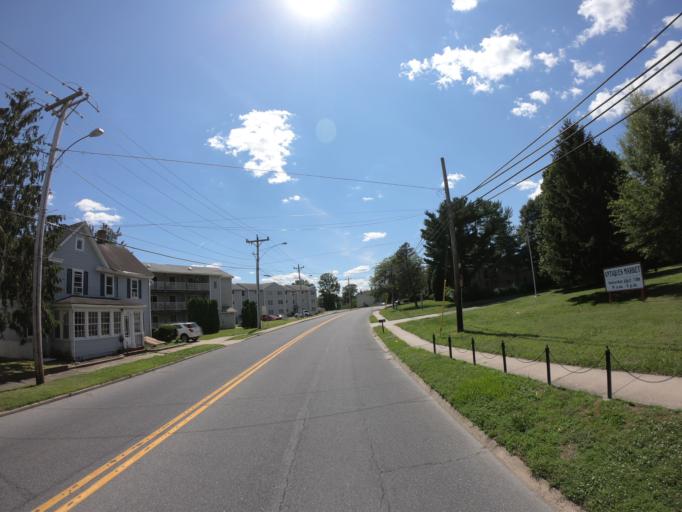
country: US
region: Delaware
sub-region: Sussex County
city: Milford
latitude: 38.9132
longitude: -75.4348
